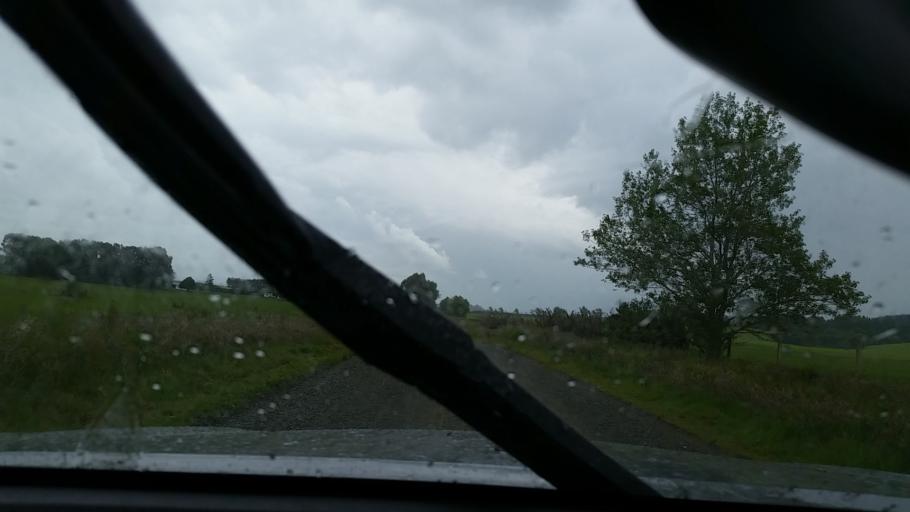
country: NZ
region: Southland
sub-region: Southland District
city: Winton
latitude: -46.0085
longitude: 168.2564
